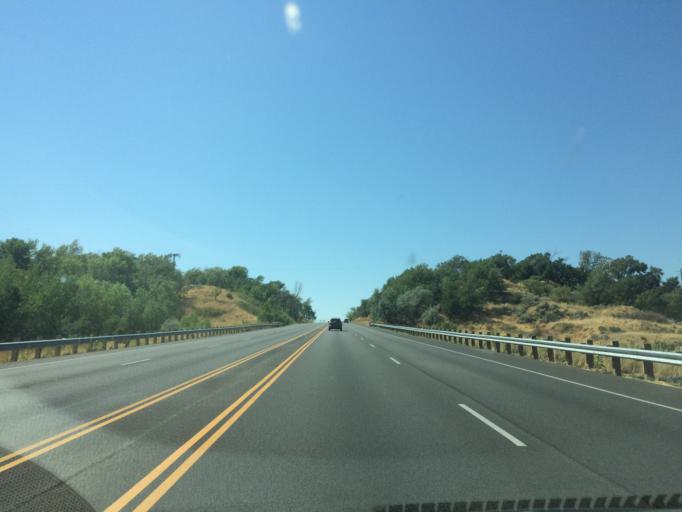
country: US
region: Utah
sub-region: Weber County
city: Ogden
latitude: 41.2357
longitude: -111.9465
